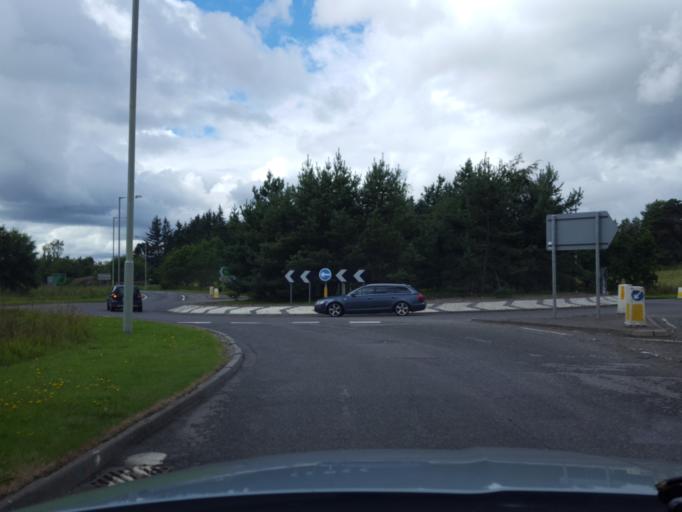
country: GB
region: Scotland
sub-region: Highland
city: Grantown on Spey
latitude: 57.3198
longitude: -3.6185
